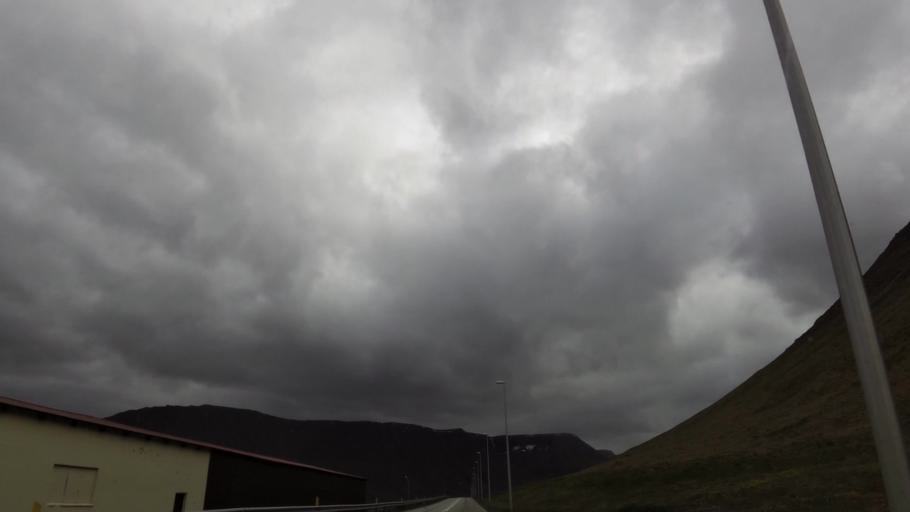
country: IS
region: Westfjords
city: Isafjoerdur
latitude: 66.1047
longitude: -23.1099
